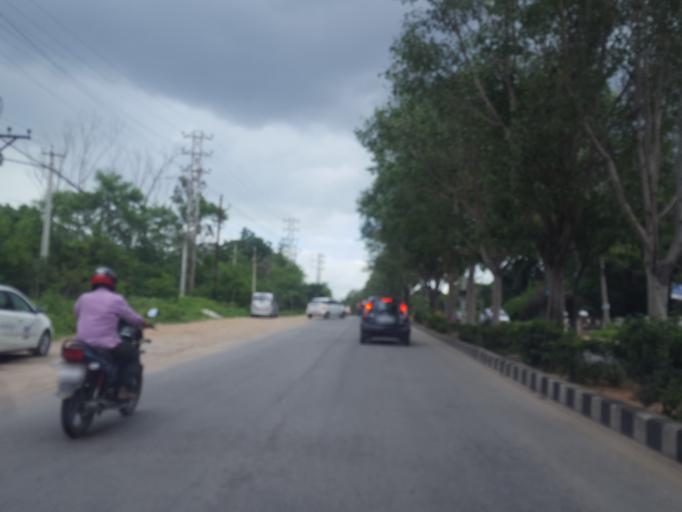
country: IN
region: Telangana
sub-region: Medak
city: Serilingampalle
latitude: 17.4623
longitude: 78.3353
